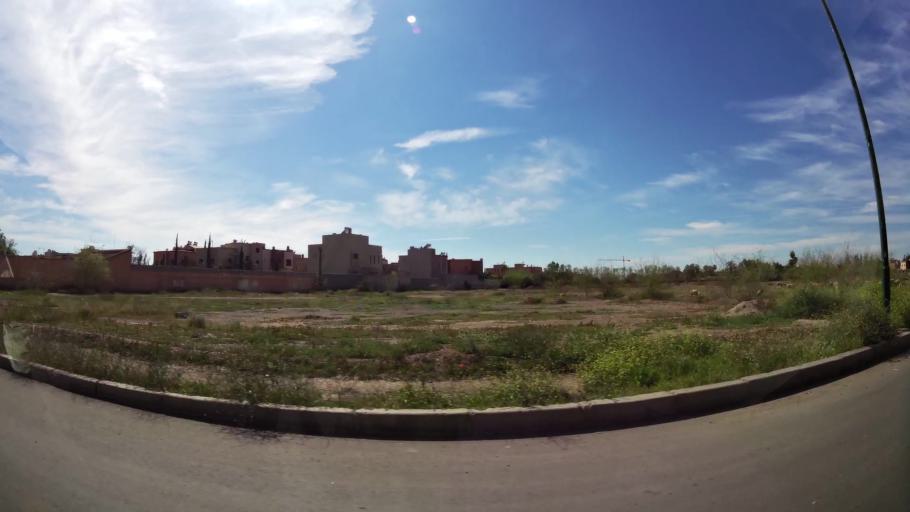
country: MA
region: Marrakech-Tensift-Al Haouz
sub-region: Marrakech
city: Marrakesh
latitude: 31.6539
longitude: -8.0601
